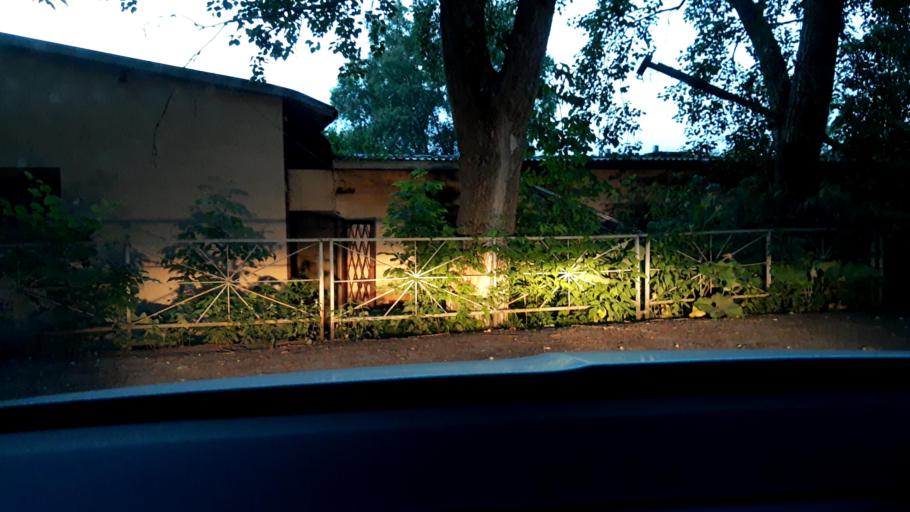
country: RU
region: Moskovskaya
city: Kur'yanovo
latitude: 55.6445
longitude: 37.6803
